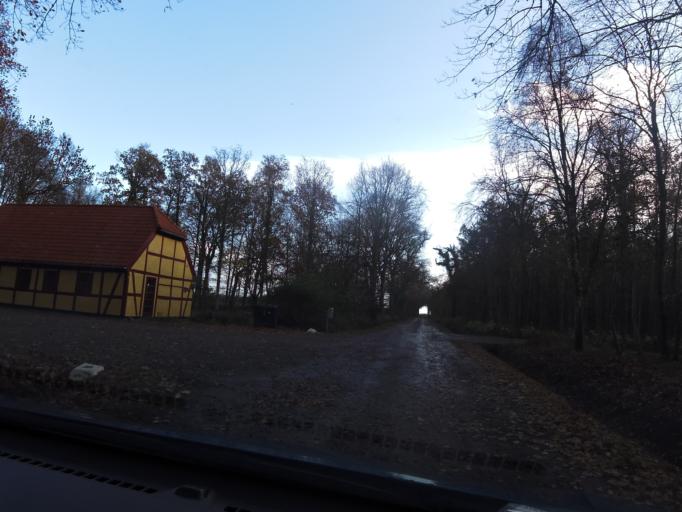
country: DK
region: Central Jutland
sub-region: Odder Kommune
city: Odder
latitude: 55.8556
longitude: 10.1627
